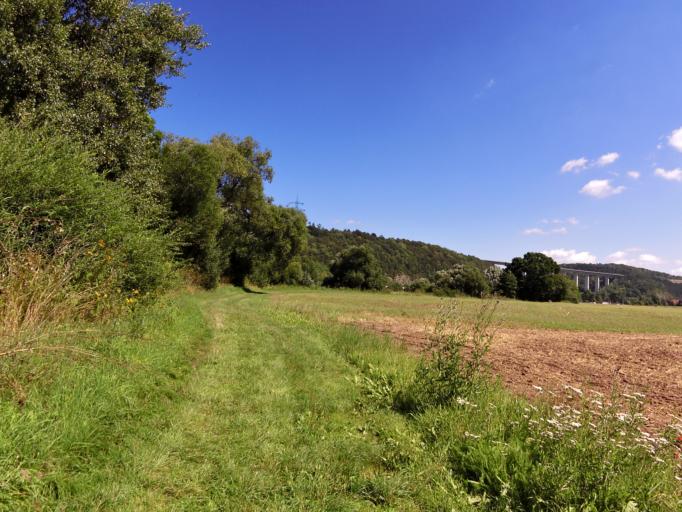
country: DE
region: Hesse
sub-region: Regierungsbezirk Kassel
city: Herleshausen
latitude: 51.0057
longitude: 10.2128
